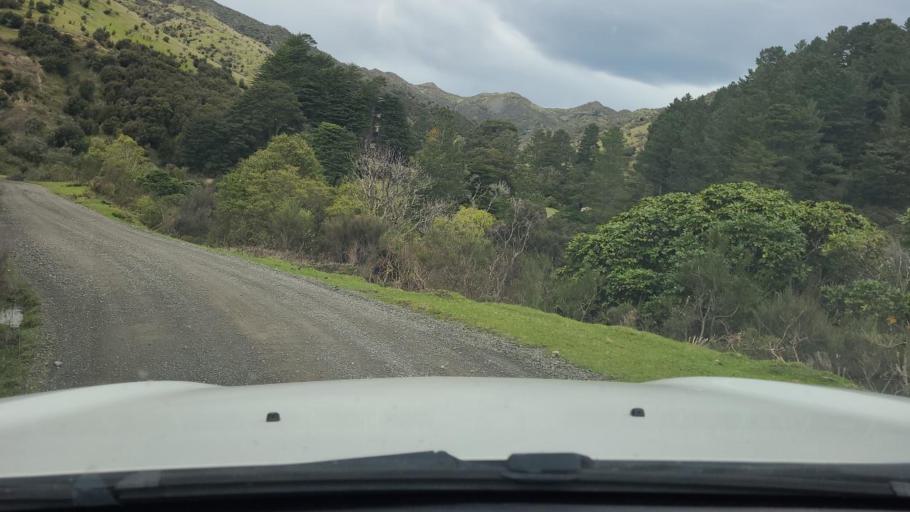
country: NZ
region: Wellington
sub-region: South Wairarapa District
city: Waipawa
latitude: -41.3875
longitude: 175.3725
